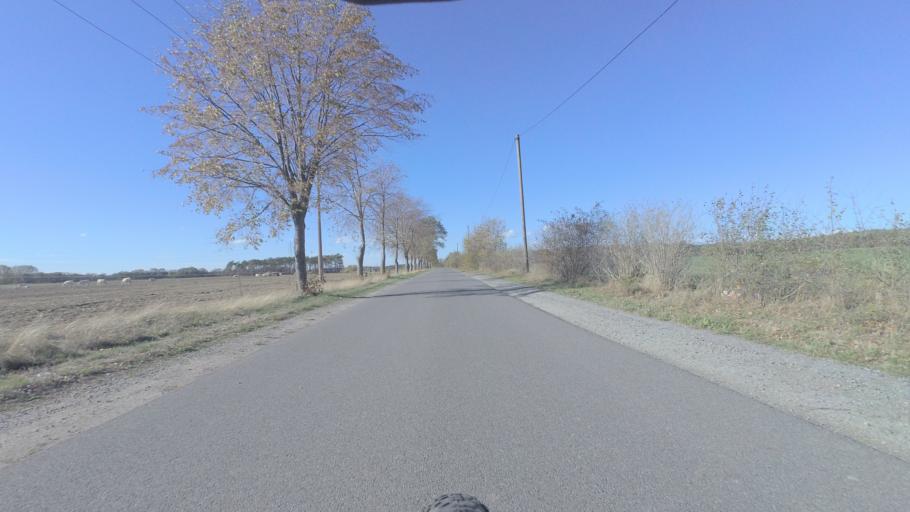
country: DE
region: Saxony
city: Nauwalde
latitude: 51.4405
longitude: 13.4419
